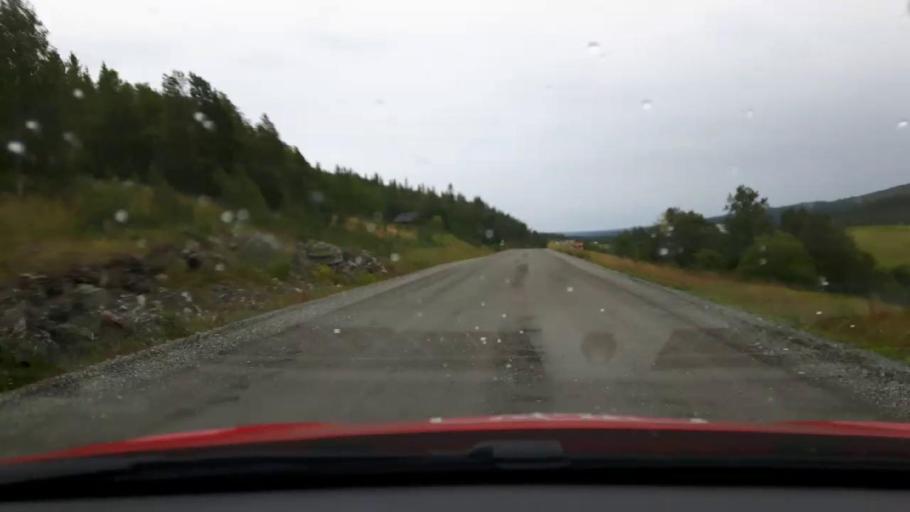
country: NO
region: Nord-Trondelag
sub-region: Meraker
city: Meraker
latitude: 63.5328
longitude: 12.3893
